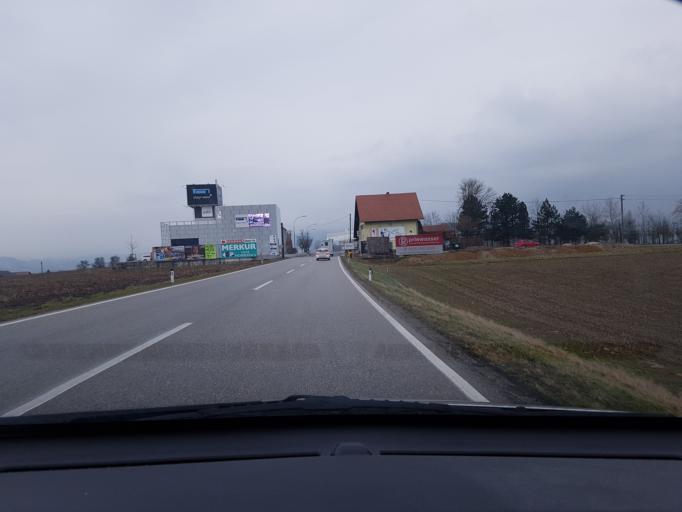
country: AT
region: Upper Austria
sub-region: Steyr Stadt
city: Steyr
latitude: 48.0531
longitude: 14.3945
